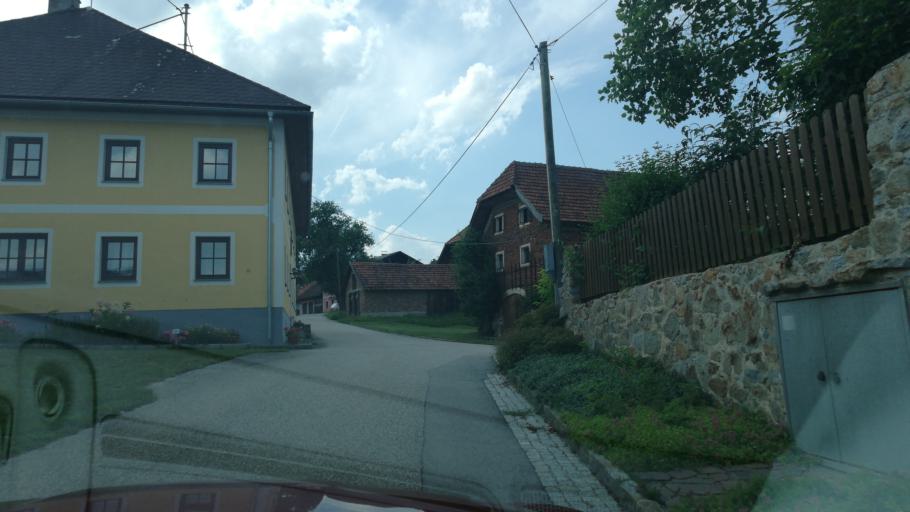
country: AT
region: Upper Austria
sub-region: Wels-Land
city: Neukirchen bei Lambach
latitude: 48.1111
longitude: 13.8232
